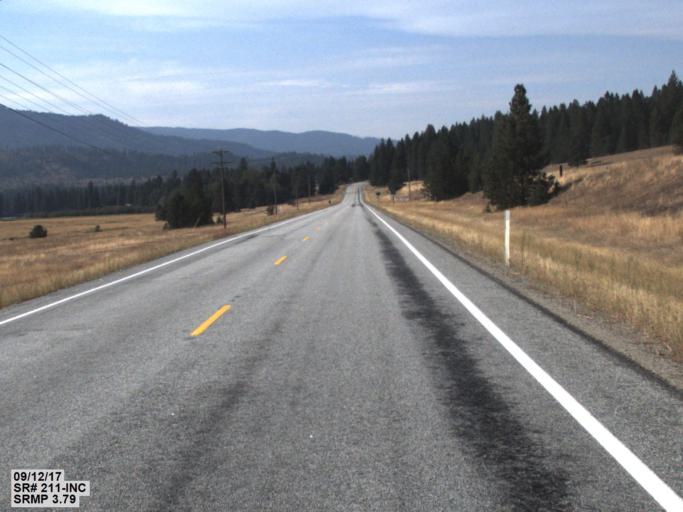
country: US
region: Washington
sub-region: Pend Oreille County
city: Newport
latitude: 48.1463
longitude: -117.2957
